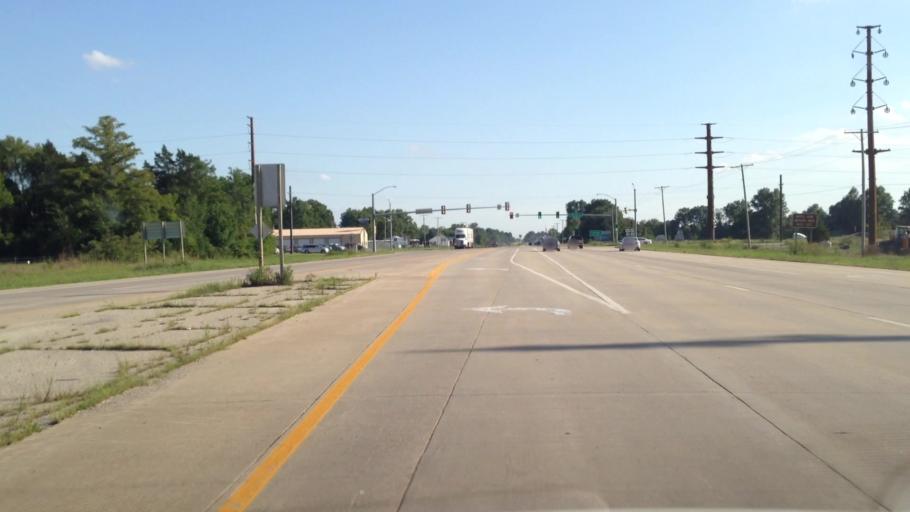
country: US
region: Kansas
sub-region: Crawford County
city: Frontenac
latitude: 37.4712
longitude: -94.7053
